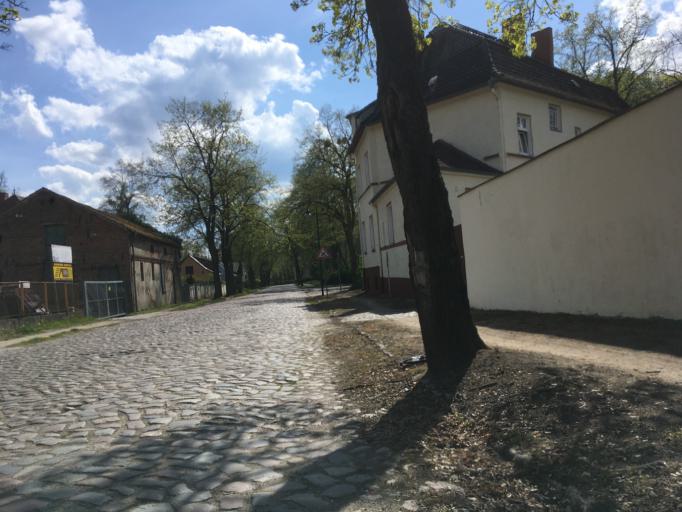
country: DE
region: Brandenburg
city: Werneuchen
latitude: 52.6364
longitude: 13.7394
